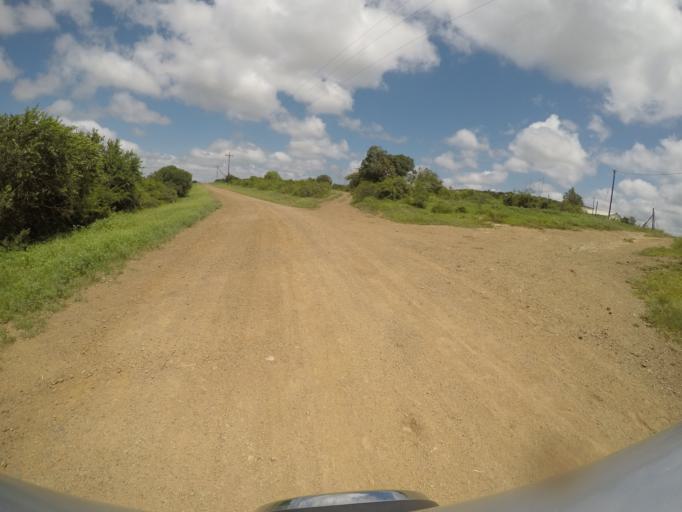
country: ZA
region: KwaZulu-Natal
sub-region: uThungulu District Municipality
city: Empangeni
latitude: -28.5880
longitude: 31.8209
